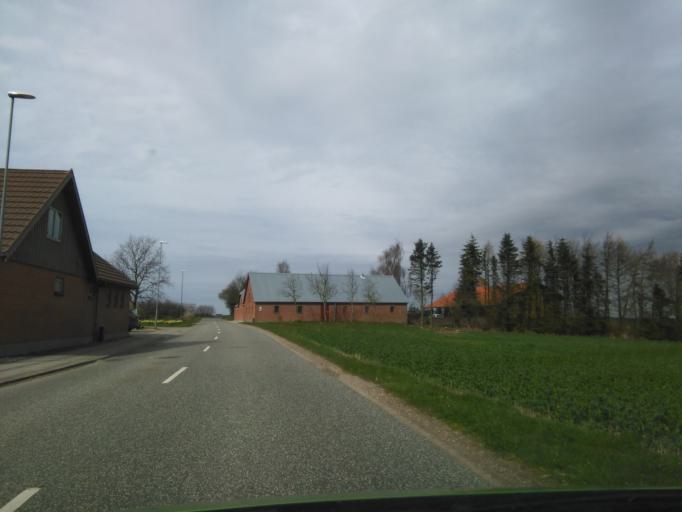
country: DK
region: Central Jutland
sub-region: Arhus Kommune
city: Solbjerg
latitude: 56.0402
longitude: 10.0673
